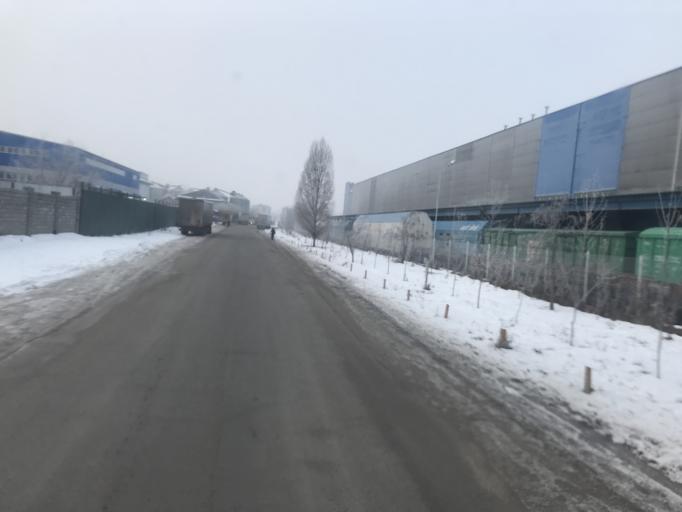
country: KZ
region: Almaty Oblysy
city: Pervomayskiy
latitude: 43.3623
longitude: 76.9785
